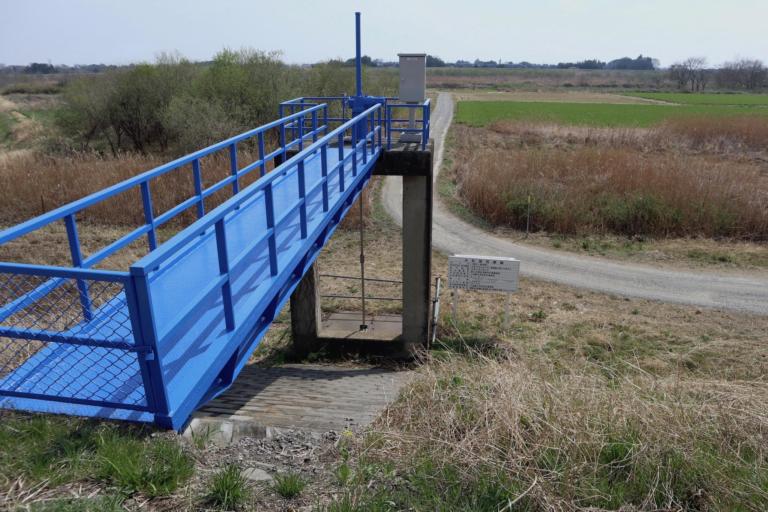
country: JP
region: Tochigi
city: Fujioka
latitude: 36.2756
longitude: 139.6195
